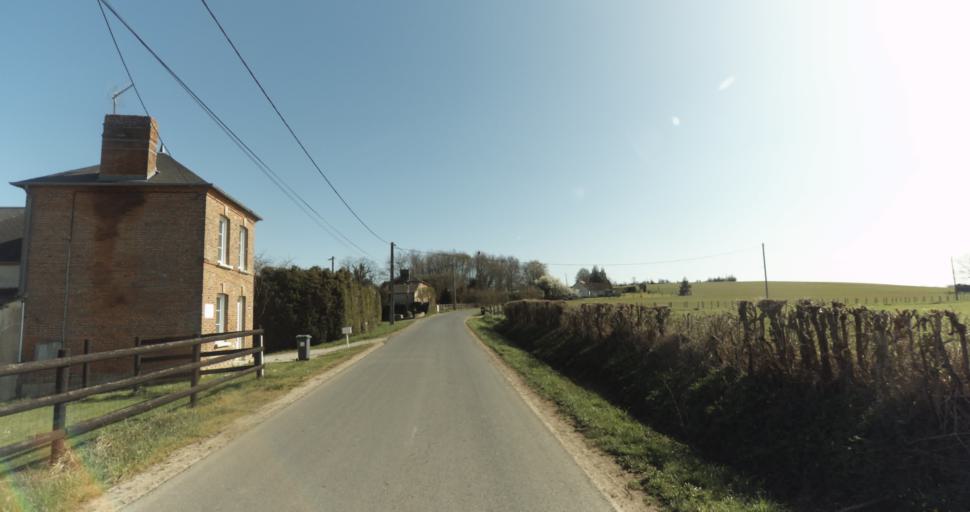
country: FR
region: Lower Normandy
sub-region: Departement de l'Orne
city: Trun
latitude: 48.9142
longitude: 0.0329
